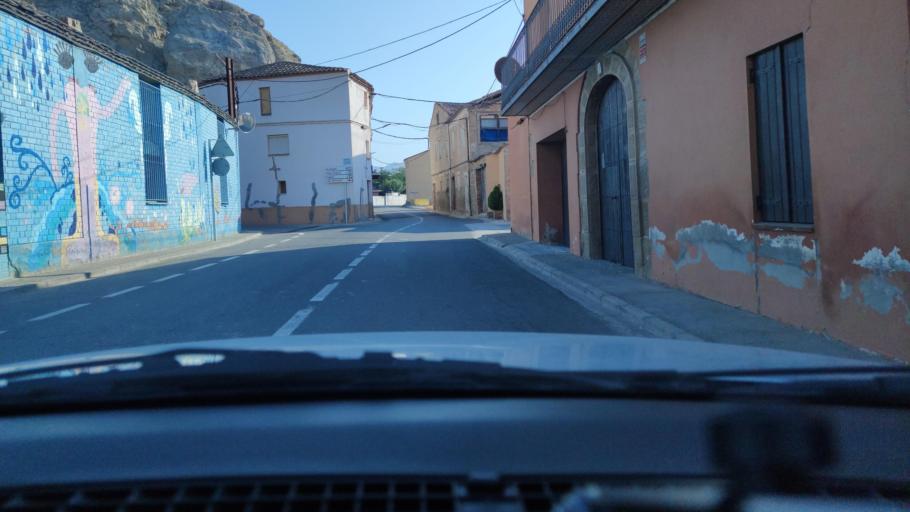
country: ES
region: Catalonia
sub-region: Provincia de Lleida
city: Balaguer
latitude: 41.8220
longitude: 0.8034
